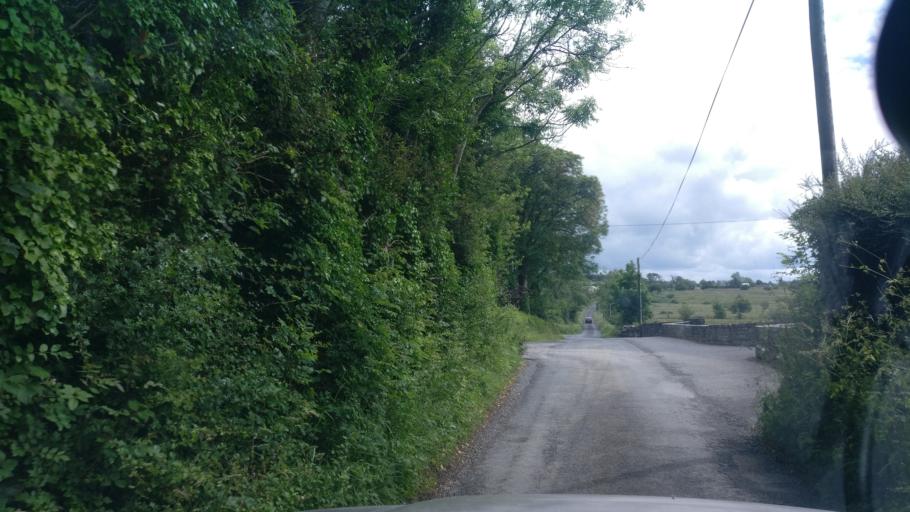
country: IE
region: Connaught
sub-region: County Galway
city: Loughrea
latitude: 53.1568
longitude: -8.5705
